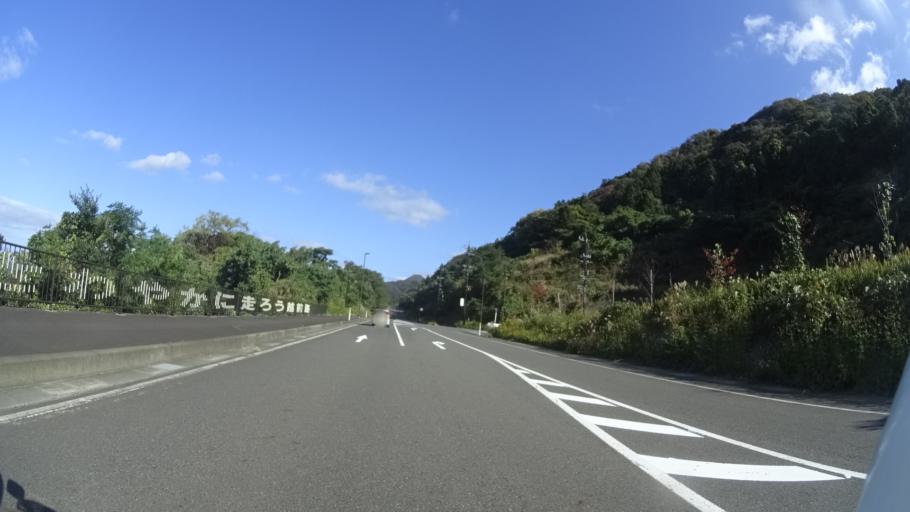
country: JP
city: Asahi
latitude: 35.9200
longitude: 135.9990
